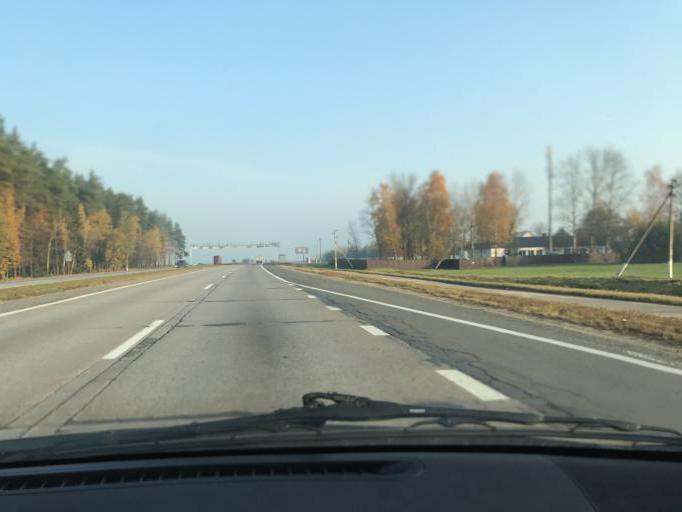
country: BY
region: Minsk
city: Borovlyany
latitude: 54.0037
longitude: 27.6571
